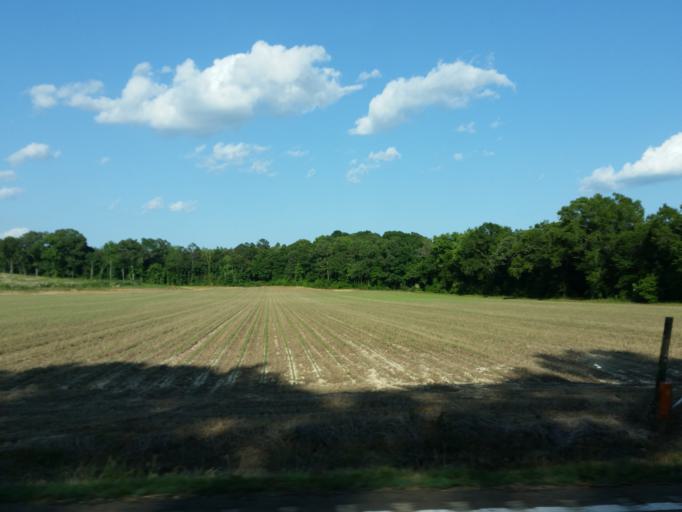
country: US
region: Mississippi
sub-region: Calhoun County
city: Calhoun City
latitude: 33.7808
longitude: -89.3641
